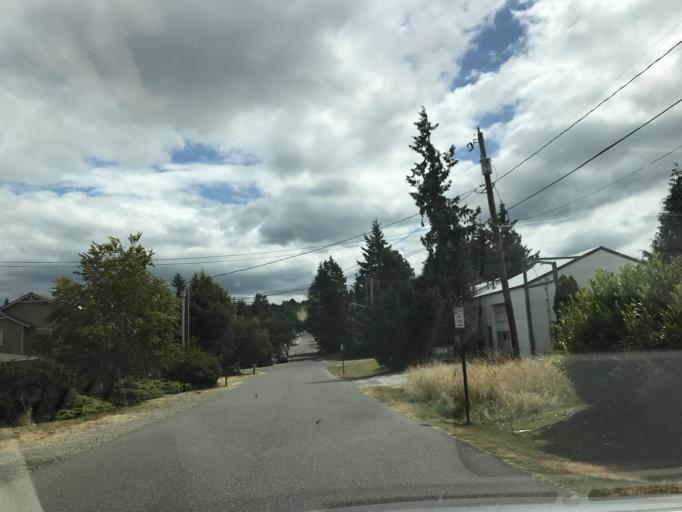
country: US
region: Washington
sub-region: Whatcom County
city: Bellingham
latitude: 48.7177
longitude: -122.5103
